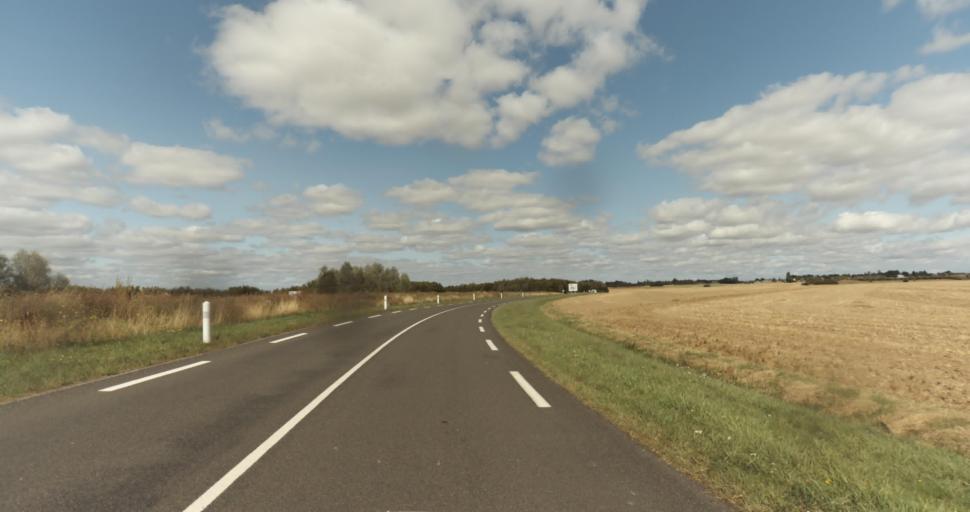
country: FR
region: Haute-Normandie
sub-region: Departement de l'Eure
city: Damville
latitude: 48.8855
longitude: 1.1743
